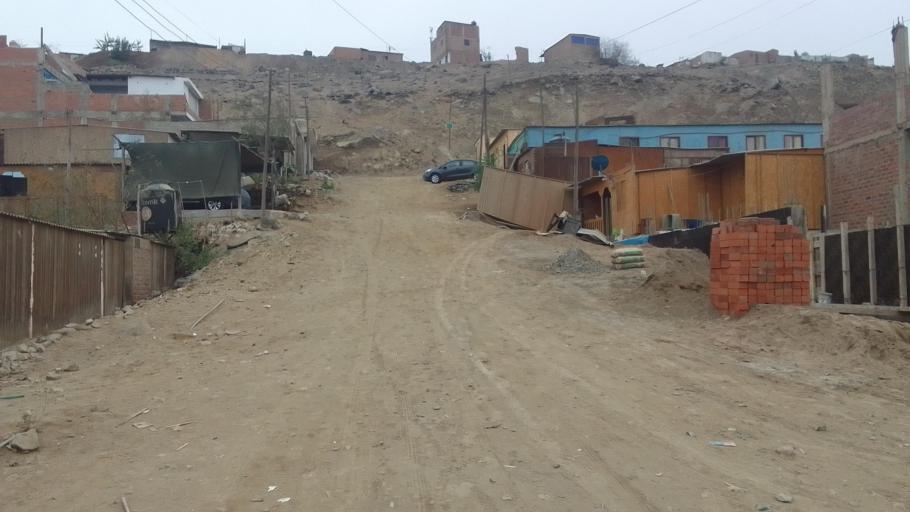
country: PE
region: Lima
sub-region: Lima
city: Santa Rosa
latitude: -11.8144
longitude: -77.1243
